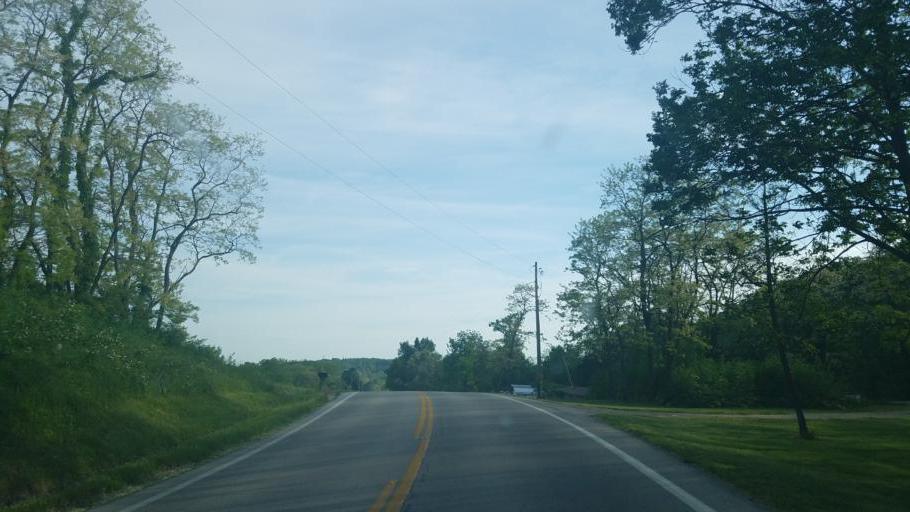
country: US
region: Ohio
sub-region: Ross County
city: Frankfort
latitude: 39.4109
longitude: -83.2789
